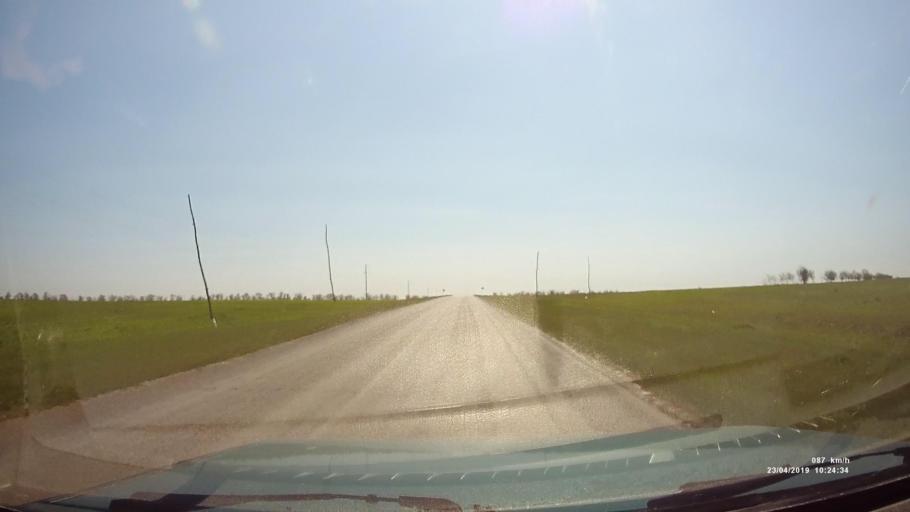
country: RU
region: Rostov
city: Sovetskoye
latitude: 46.6375
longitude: 42.4442
